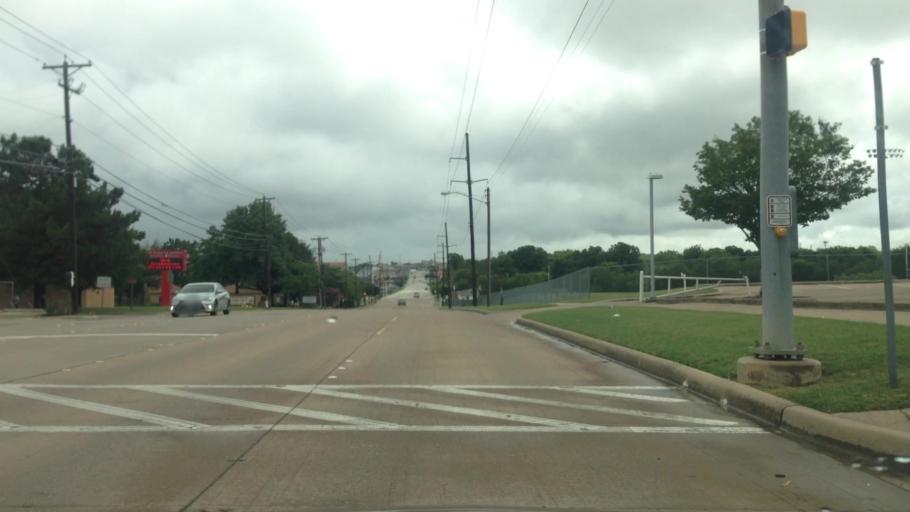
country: US
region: Texas
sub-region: Tarrant County
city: White Settlement
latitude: 32.7483
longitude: -97.4518
